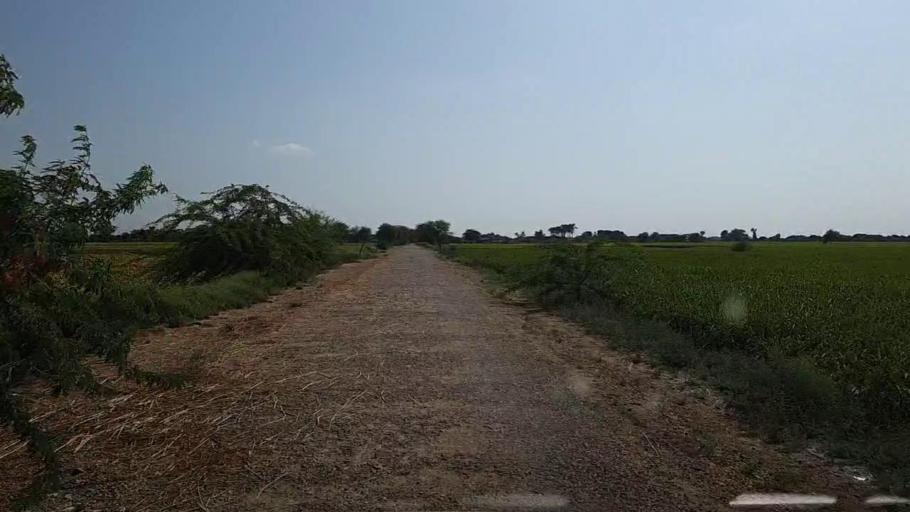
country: PK
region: Sindh
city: Kario
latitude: 24.8192
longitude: 68.5450
